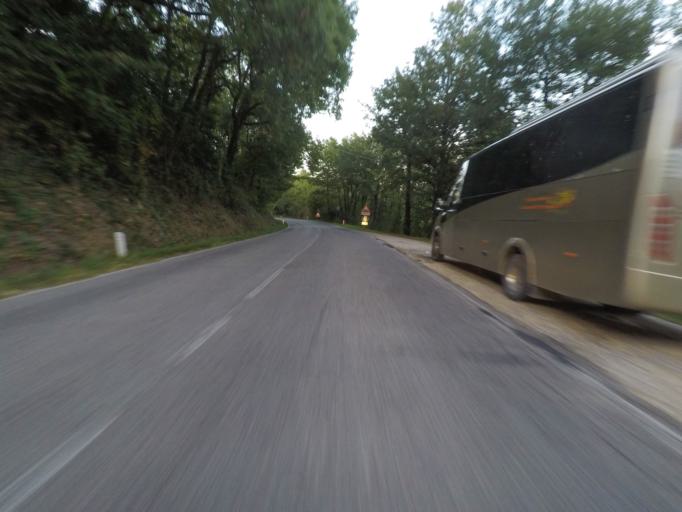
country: IT
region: Tuscany
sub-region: Provincia di Siena
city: Torrita di Siena
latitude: 43.1352
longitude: 11.7302
